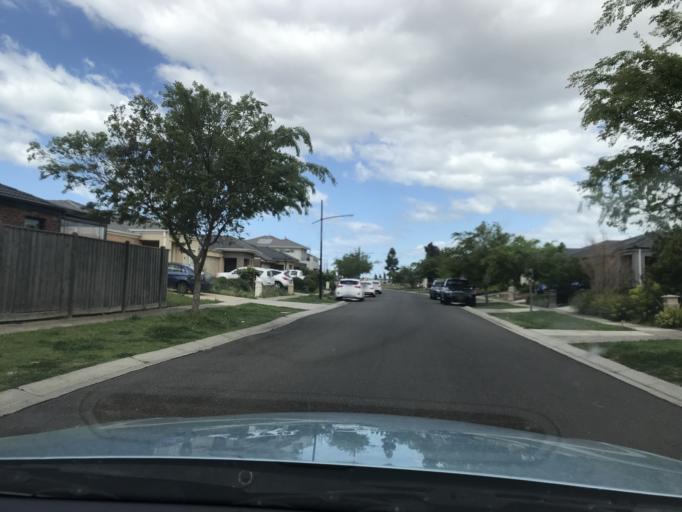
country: AU
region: Victoria
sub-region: Wyndham
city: Williams Landing
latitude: -37.8612
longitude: 144.7456
